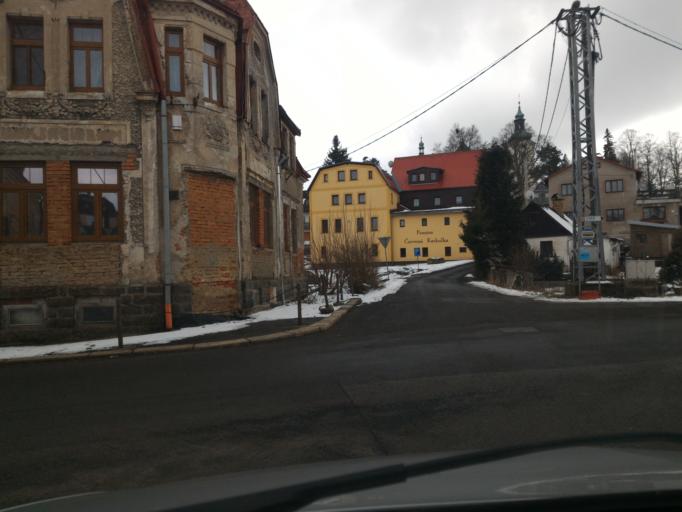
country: CZ
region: Liberecky
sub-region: Okres Jablonec nad Nisou
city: Smrzovka
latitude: 50.7319
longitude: 15.2415
